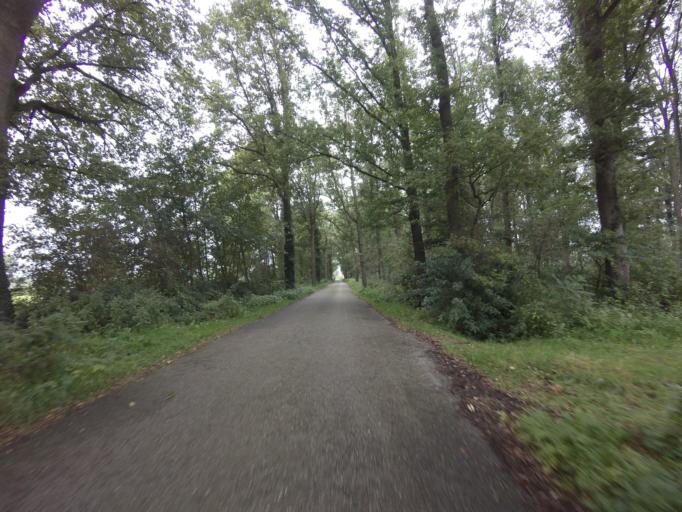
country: NL
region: Overijssel
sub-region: Gemeente Enschede
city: Enschede
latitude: 52.1929
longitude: 6.9252
